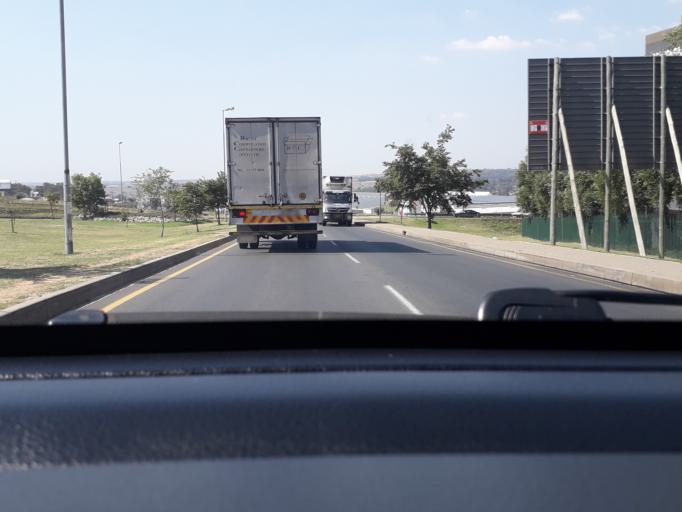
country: ZA
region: Gauteng
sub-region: City of Johannesburg Metropolitan Municipality
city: Modderfontein
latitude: -26.1061
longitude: 28.1375
